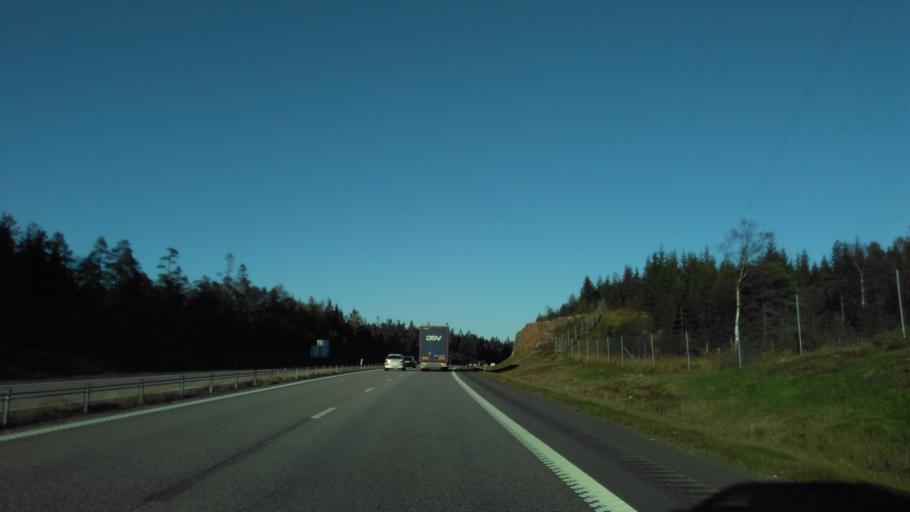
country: SE
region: Vaestra Goetaland
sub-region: Boras Kommun
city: Dalsjofors
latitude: 57.7495
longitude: 13.0722
